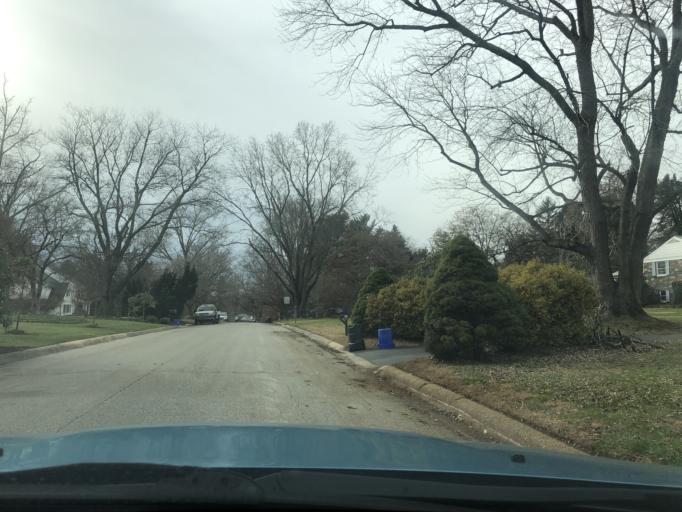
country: US
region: Pennsylvania
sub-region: Delaware County
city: Radnor
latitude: 40.0249
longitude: -75.3542
